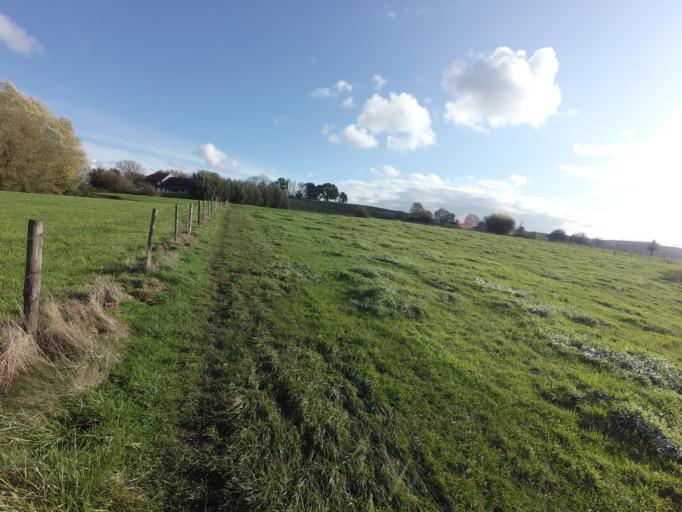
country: BE
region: Wallonia
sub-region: Province de Liege
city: Plombieres
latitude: 50.7606
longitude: 5.9139
